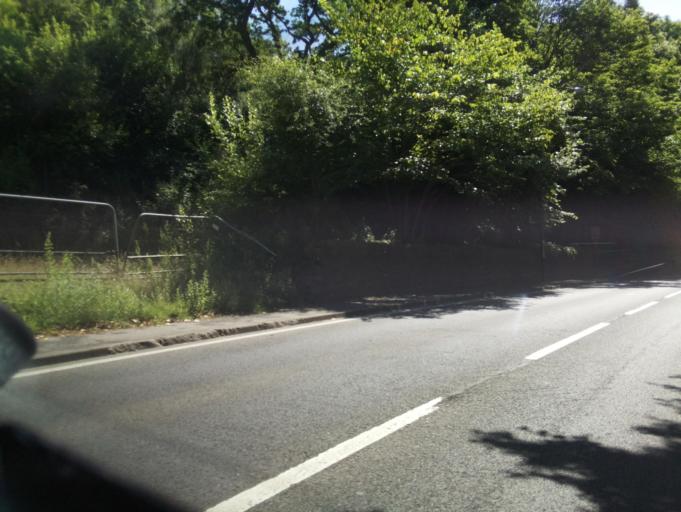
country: GB
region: England
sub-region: Derbyshire
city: Matlock
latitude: 53.1692
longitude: -1.6034
